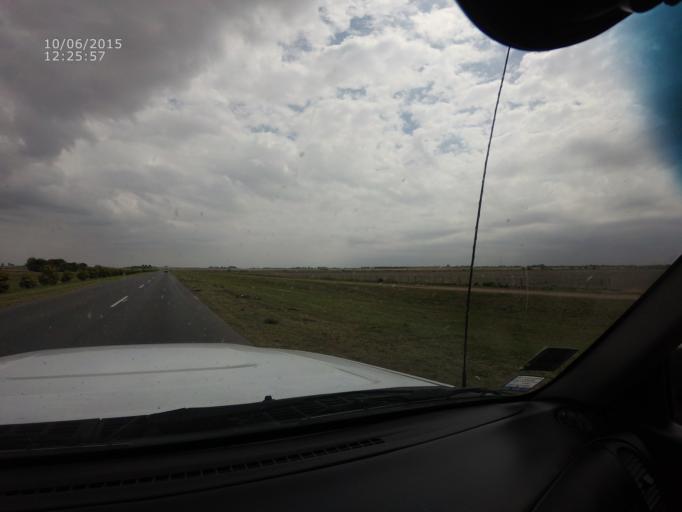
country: AR
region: Santa Fe
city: Roldan
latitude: -32.9049
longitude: -61.0085
